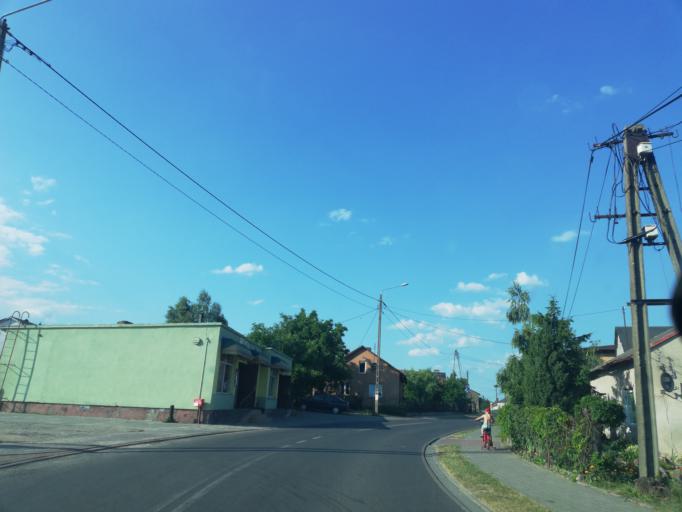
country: PL
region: Kujawsko-Pomorskie
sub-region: Powiat golubsko-dobrzynski
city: Golub-Dobrzyn
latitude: 53.0161
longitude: 19.0559
